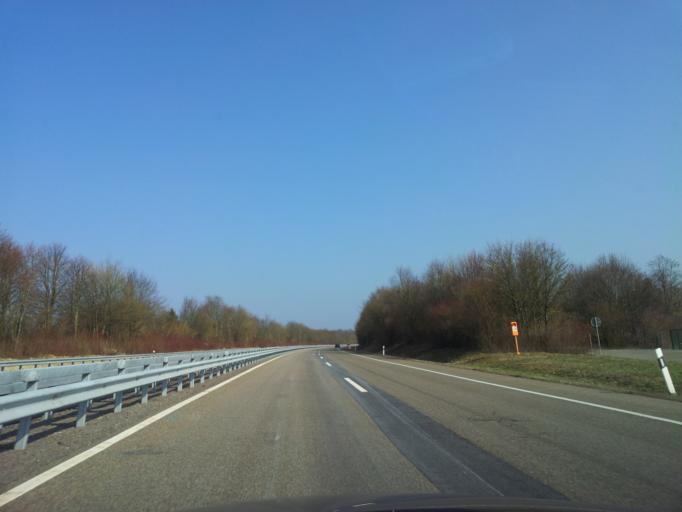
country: DE
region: Rheinland-Pfalz
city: Hoheinod
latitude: 49.2856
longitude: 7.6140
